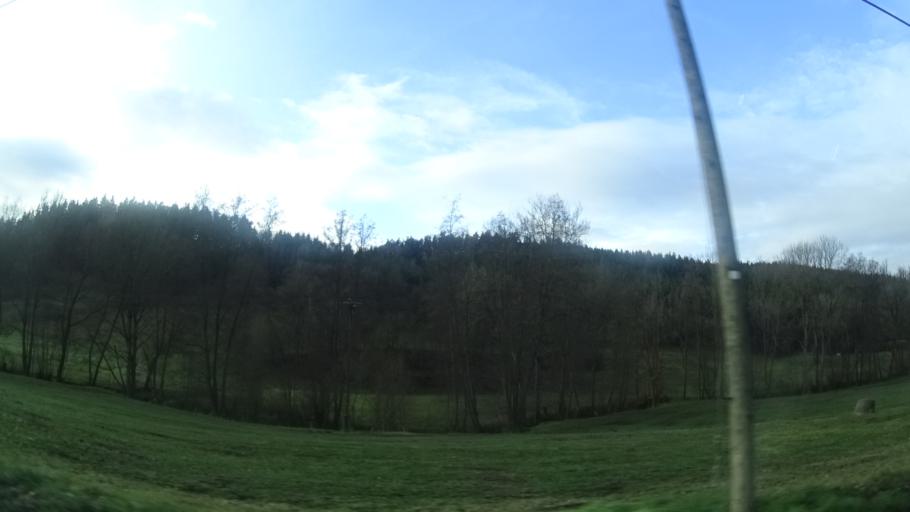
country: DE
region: Thuringia
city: Rottenbach
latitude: 50.7009
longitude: 11.2044
